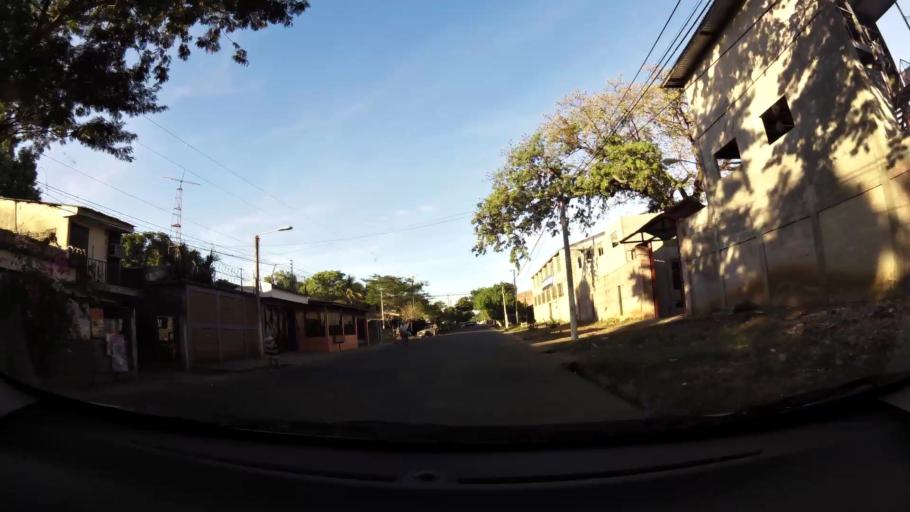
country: SV
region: San Miguel
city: San Miguel
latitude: 13.4644
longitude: -88.1762
